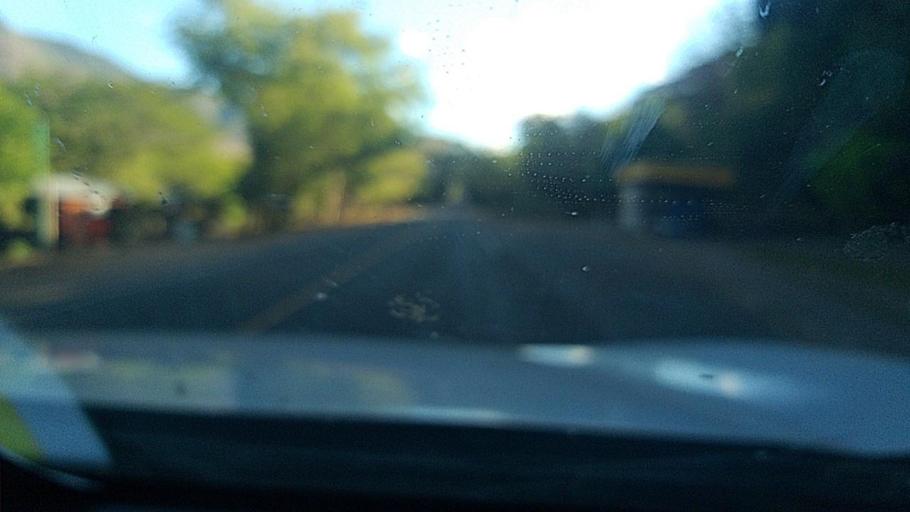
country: NI
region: Esteli
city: Condega
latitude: 13.2991
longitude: -86.3496
